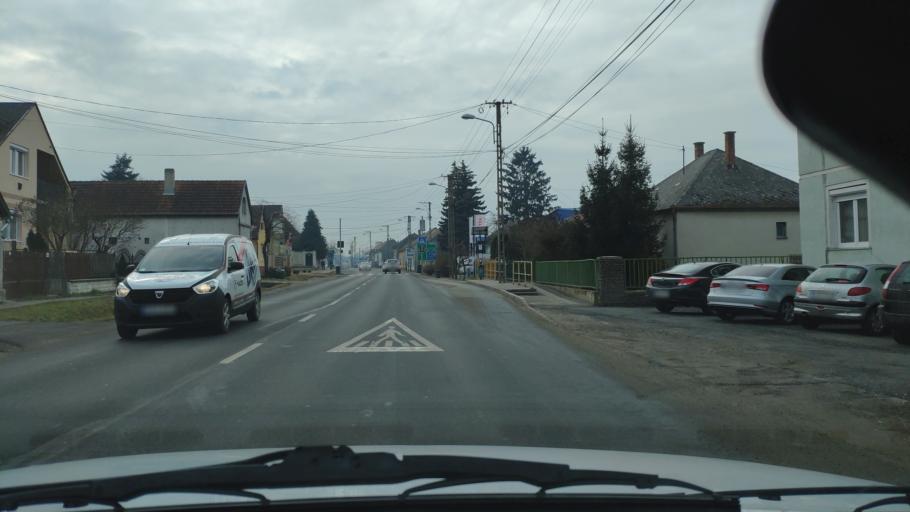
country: HU
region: Zala
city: Nagykanizsa
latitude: 46.4694
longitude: 16.9857
